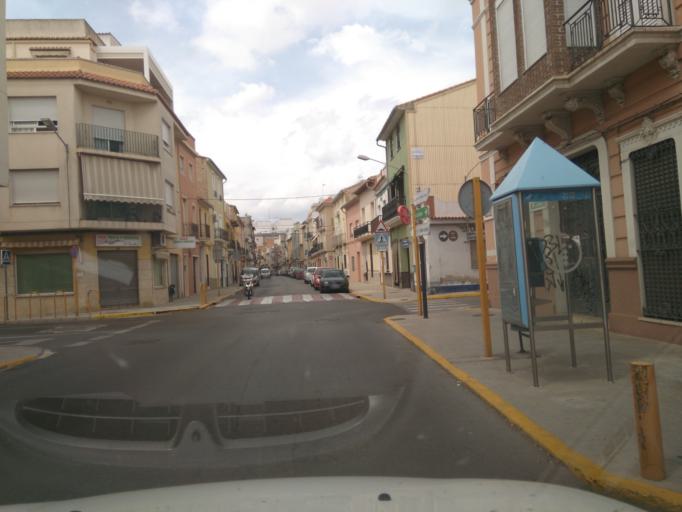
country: ES
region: Valencia
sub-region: Provincia de Valencia
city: Carcaixent
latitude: 39.1193
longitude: -0.4444
